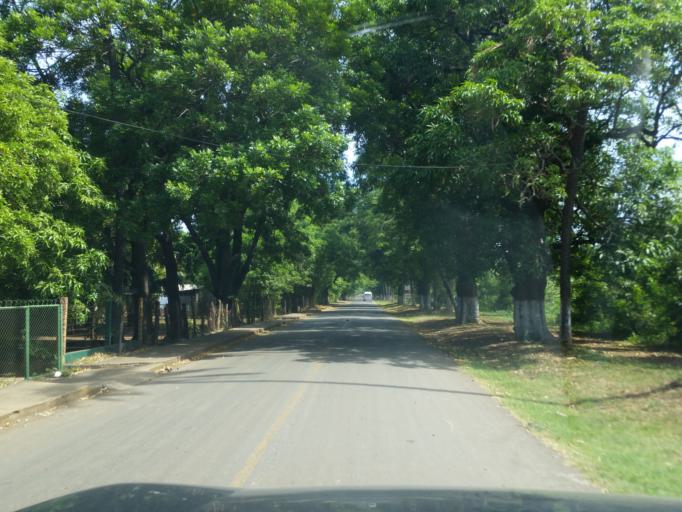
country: NI
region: Managua
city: Masachapa
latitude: 11.7896
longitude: -86.5135
